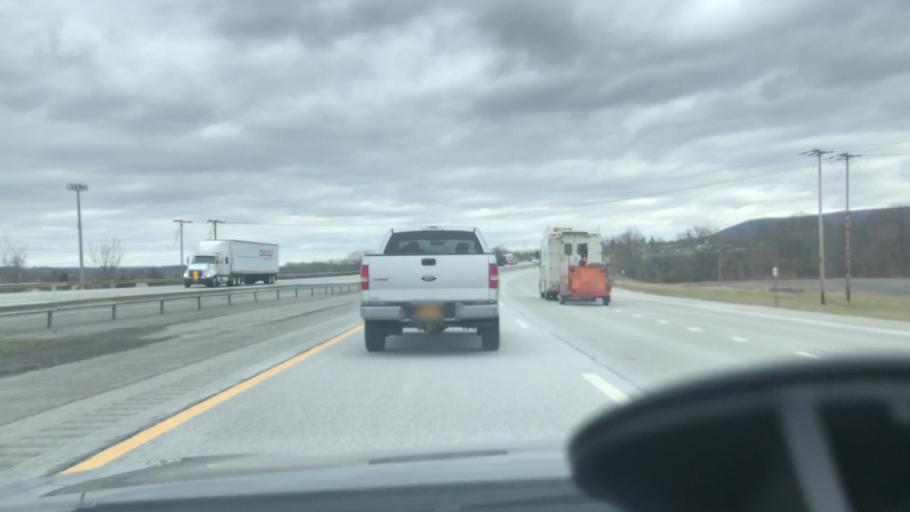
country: US
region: New York
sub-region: Herkimer County
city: Herkimer
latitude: 43.0178
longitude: -74.9869
